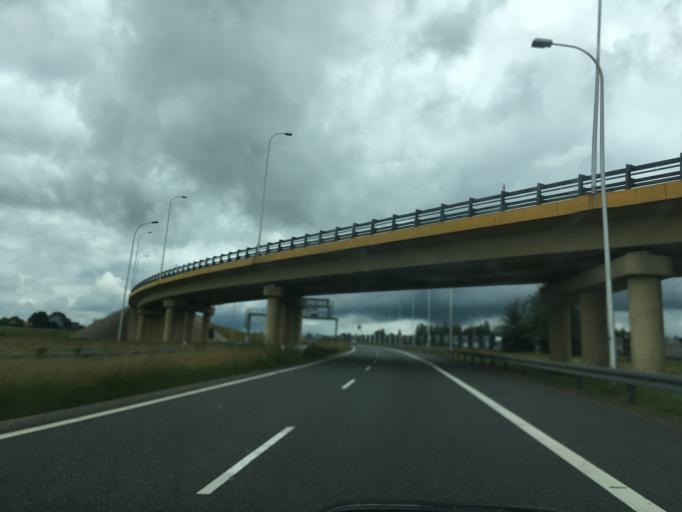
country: PL
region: Lublin Voivodeship
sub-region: Powiat swidnicki
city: Swidnik
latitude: 51.2082
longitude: 22.6574
